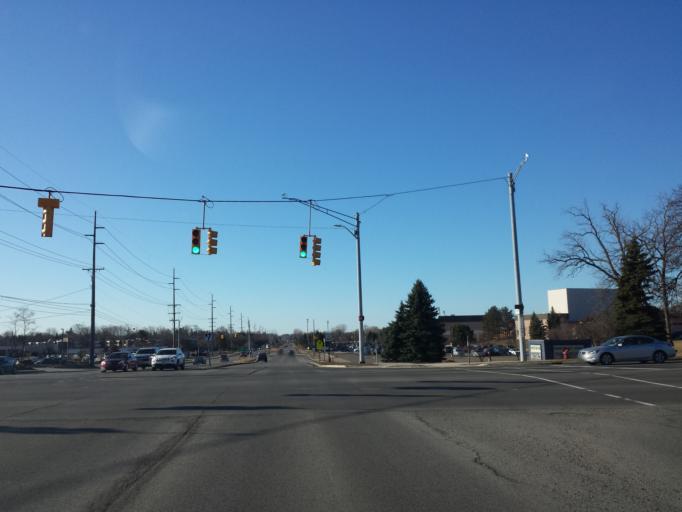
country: US
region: Michigan
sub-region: Oakland County
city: Rochester
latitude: 42.6818
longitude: -83.1536
